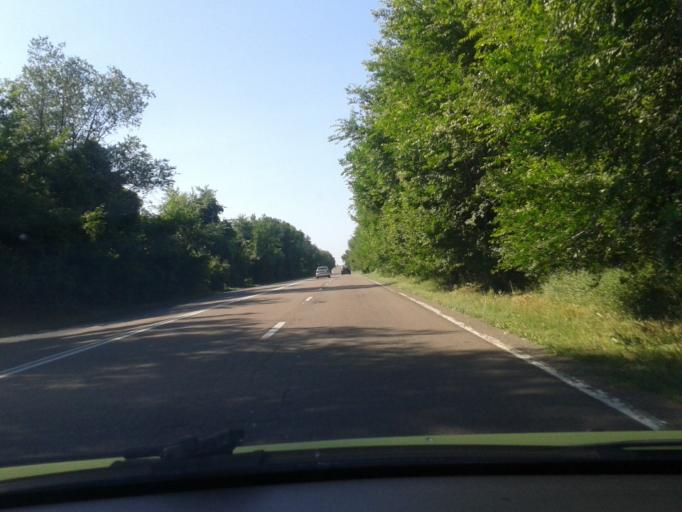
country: RO
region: Constanta
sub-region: Comuna Douazeci si Trei August
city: Dulcesti
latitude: 43.8655
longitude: 28.5750
